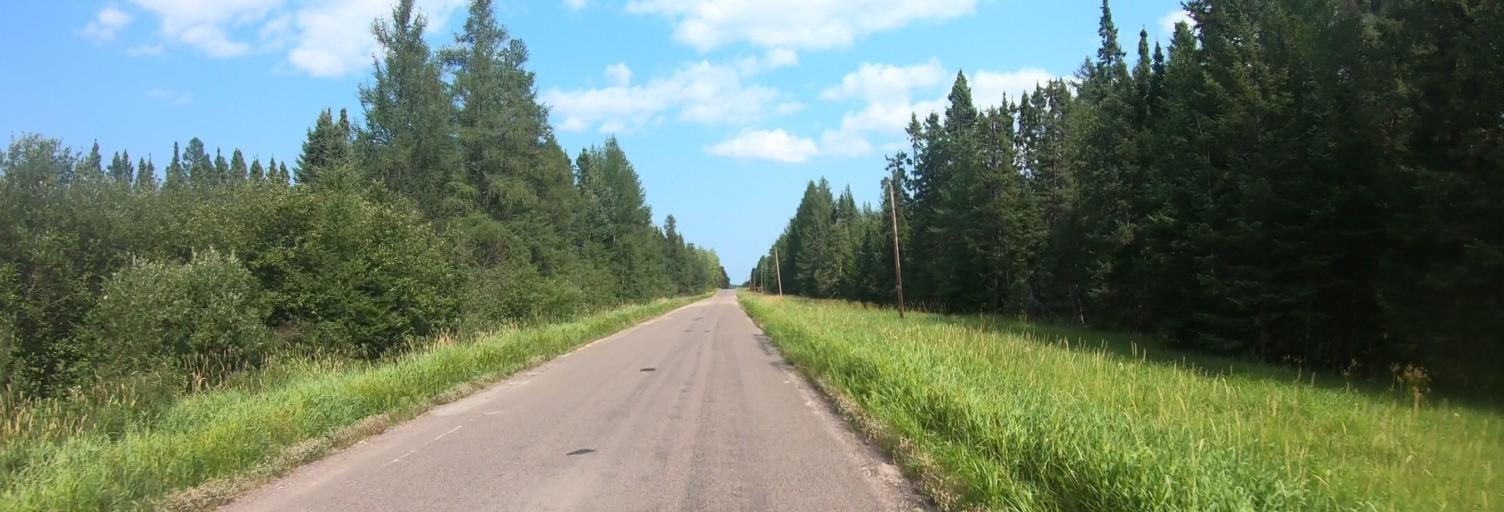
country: US
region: Minnesota
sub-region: Saint Louis County
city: Mountain Iron
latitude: 47.8920
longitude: -92.6985
